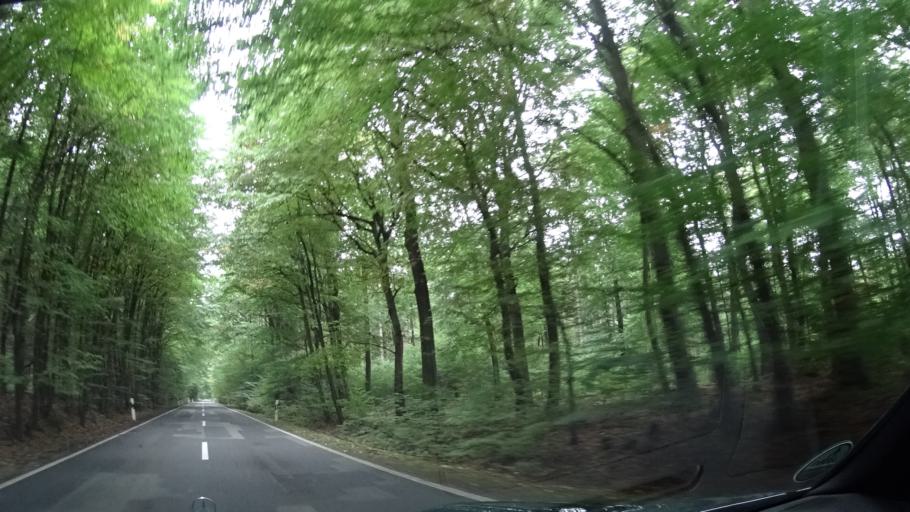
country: DE
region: Brandenburg
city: Walsleben
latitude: 52.9760
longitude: 12.7139
